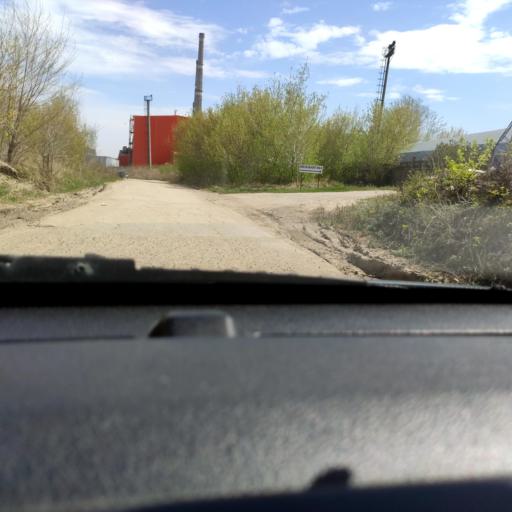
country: RU
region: Samara
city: Podstepki
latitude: 53.5761
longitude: 49.2285
